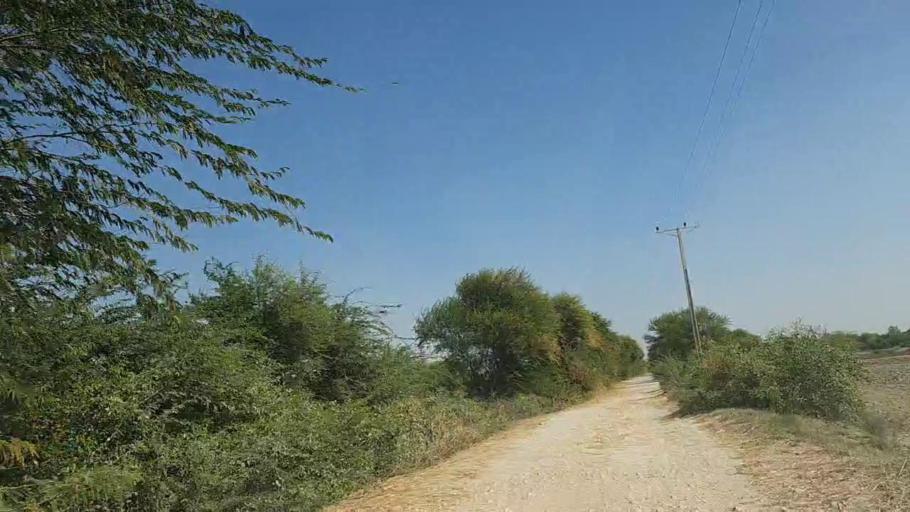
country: PK
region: Sindh
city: Mirpur Batoro
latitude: 24.7324
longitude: 68.2364
